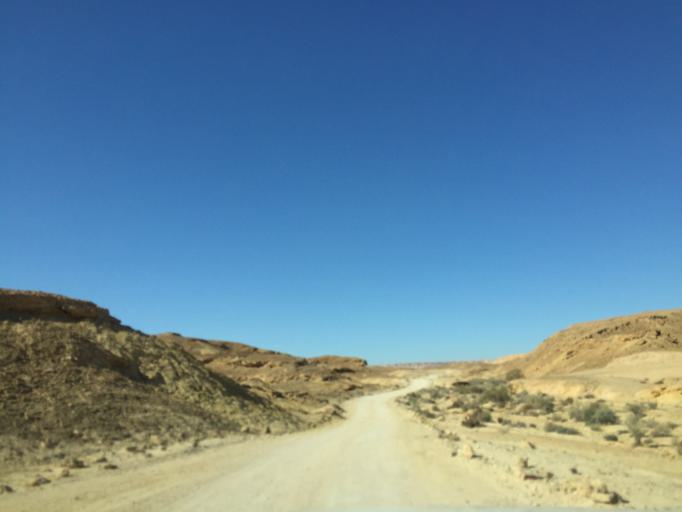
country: IL
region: Southern District
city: Mitzpe Ramon
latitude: 30.6068
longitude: 34.9385
